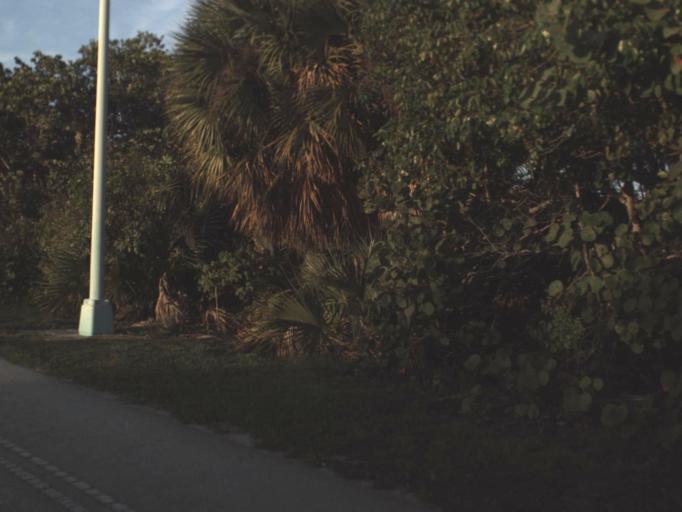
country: US
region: Florida
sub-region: Miami-Dade County
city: Key Biscayne
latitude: 25.7232
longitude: -80.1509
